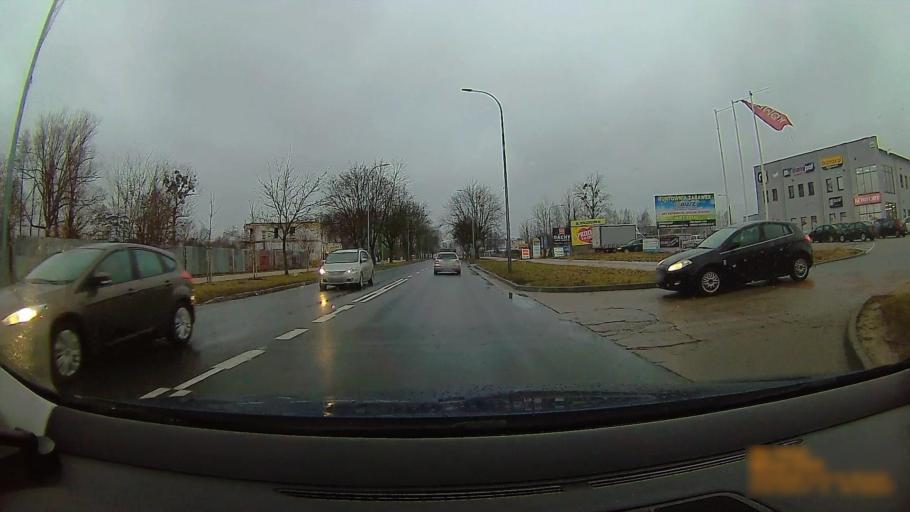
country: PL
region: Greater Poland Voivodeship
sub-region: Konin
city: Konin
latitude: 52.2325
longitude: 18.2284
